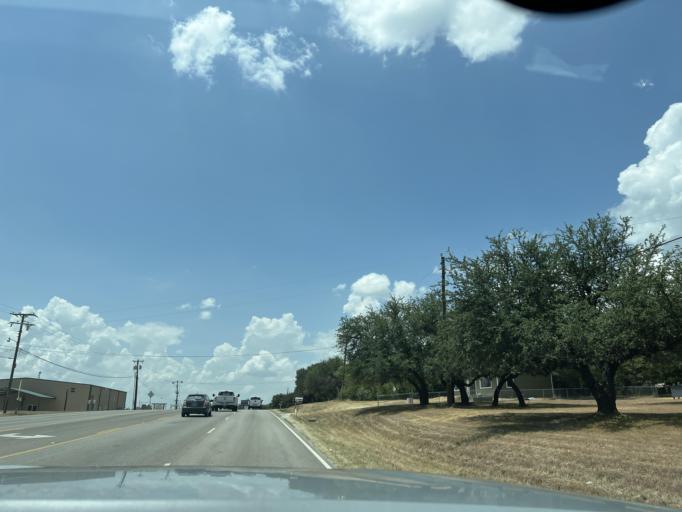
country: US
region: Texas
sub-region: Parker County
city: Weatherford
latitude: 32.7866
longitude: -97.7959
